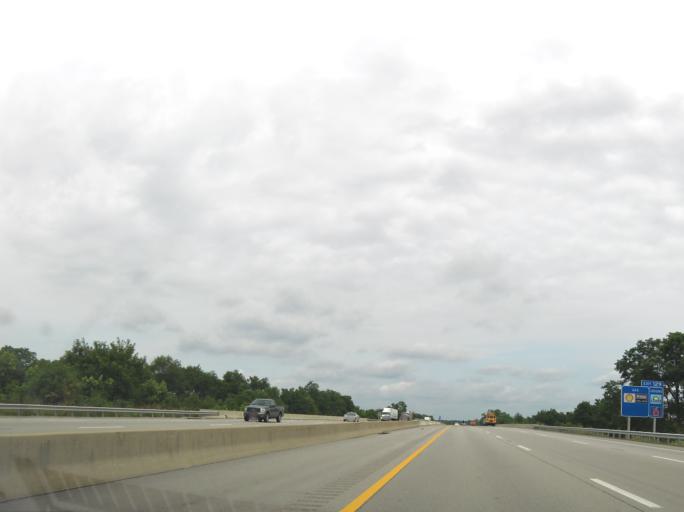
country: US
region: Kentucky
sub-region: Scott County
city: Georgetown
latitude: 38.2635
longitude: -84.5529
